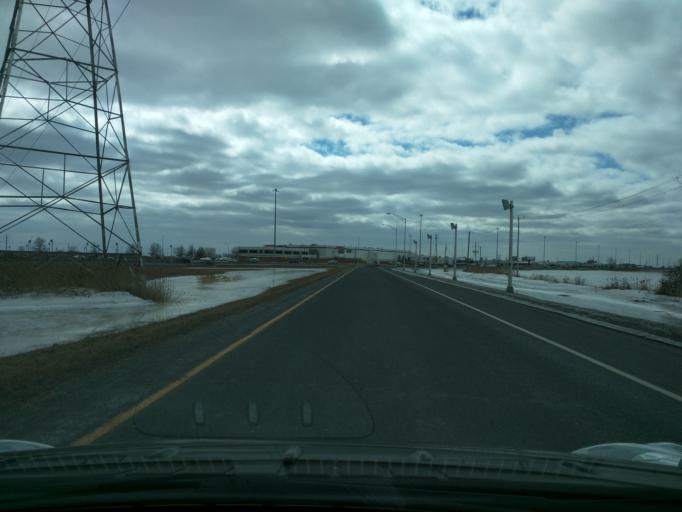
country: CA
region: Quebec
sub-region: Monteregie
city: Sainte-Julie
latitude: 45.5747
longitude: -73.3751
